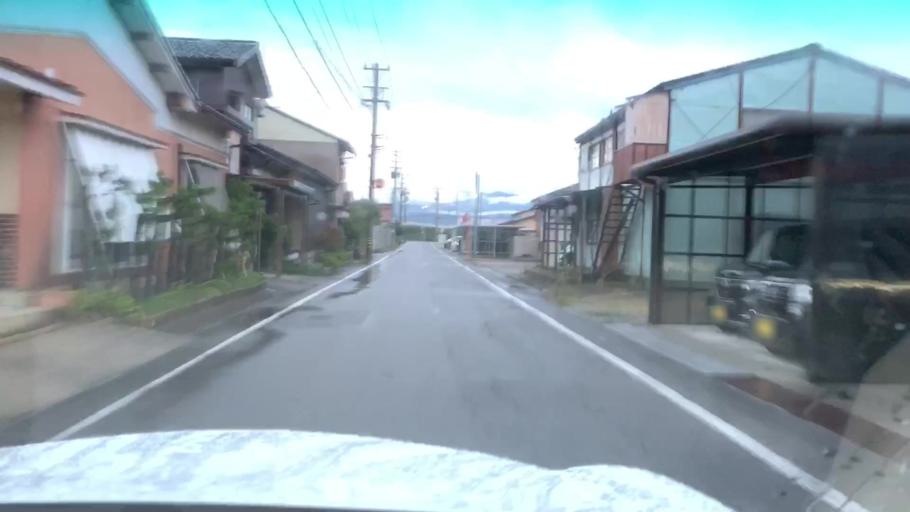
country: JP
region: Toyama
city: Kamiichi
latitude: 36.7042
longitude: 137.3355
